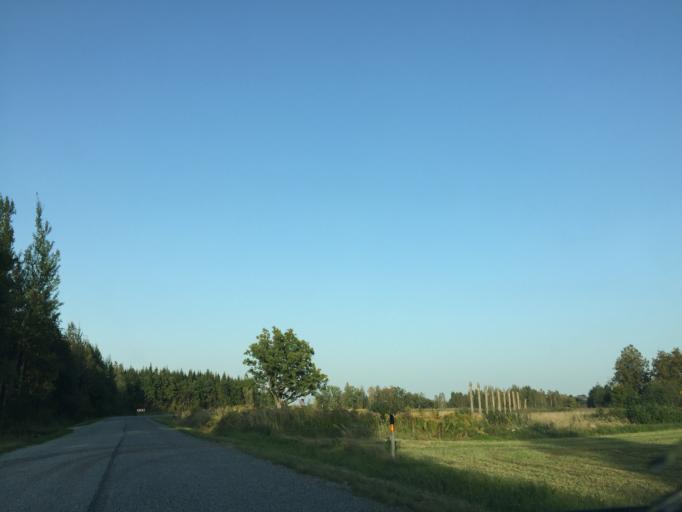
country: LV
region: Kegums
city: Kegums
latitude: 56.8223
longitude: 24.7536
